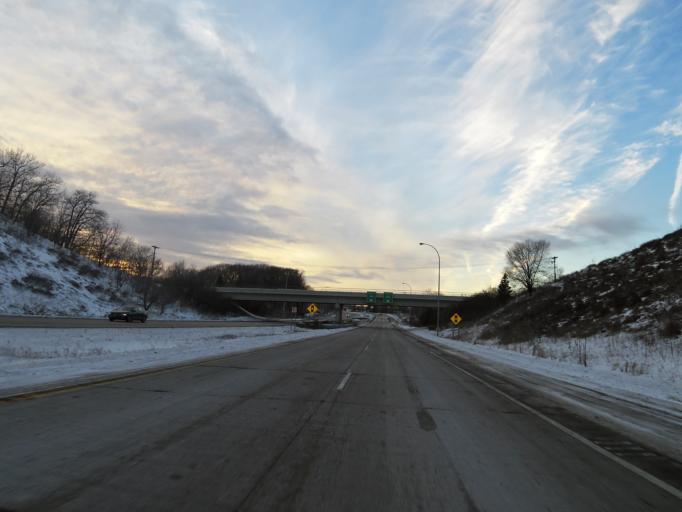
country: US
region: Minnesota
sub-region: Hennepin County
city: Hopkins
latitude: 44.8922
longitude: -93.4312
